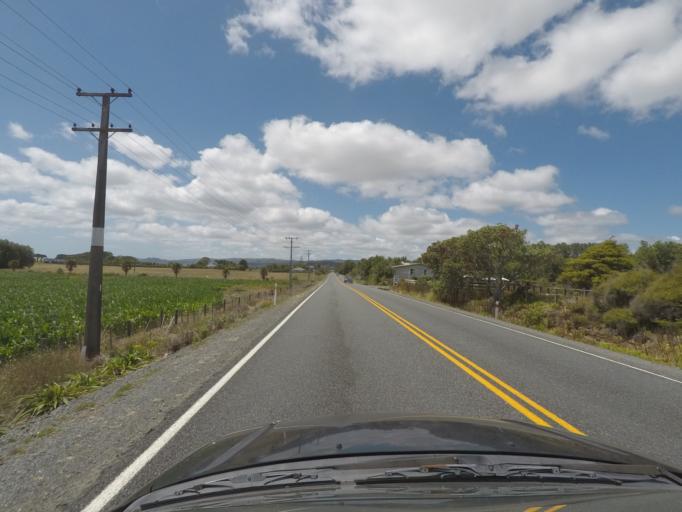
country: NZ
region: Northland
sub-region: Whangarei
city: Ruakaka
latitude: -36.0005
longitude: 174.4753
